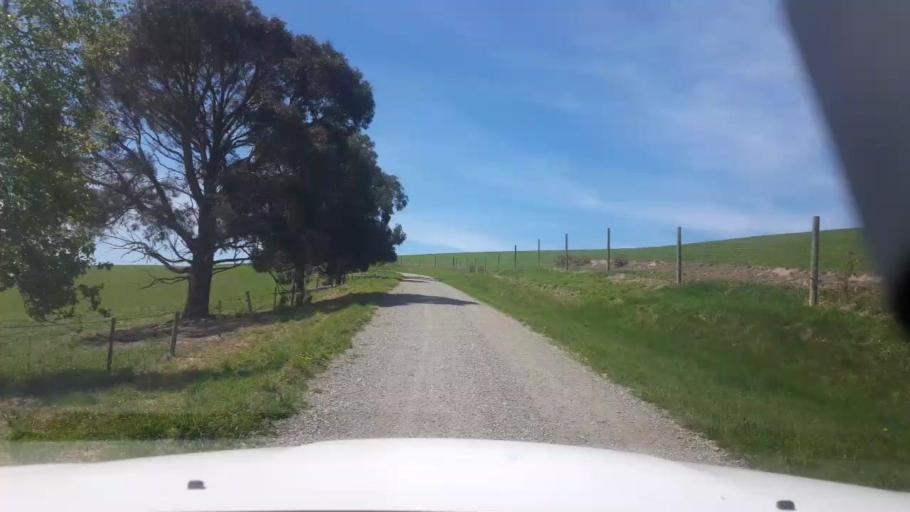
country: NZ
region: Canterbury
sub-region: Timaru District
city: Pleasant Point
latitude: -44.3103
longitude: 171.0976
